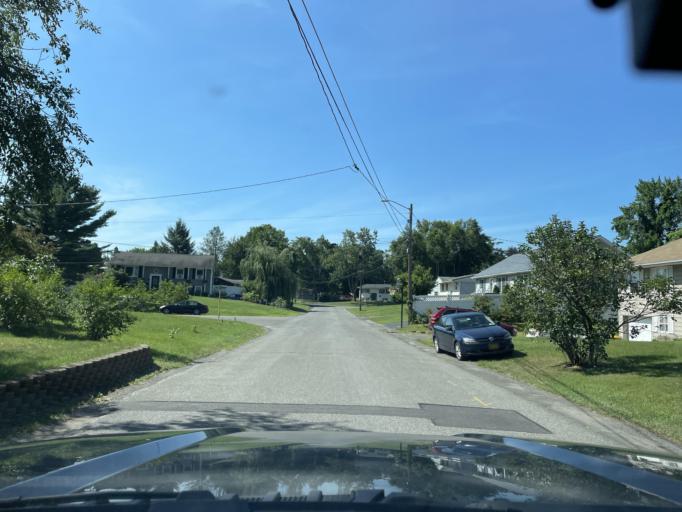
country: US
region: New York
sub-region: Ulster County
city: Saugerties South
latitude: 42.0656
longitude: -73.9575
